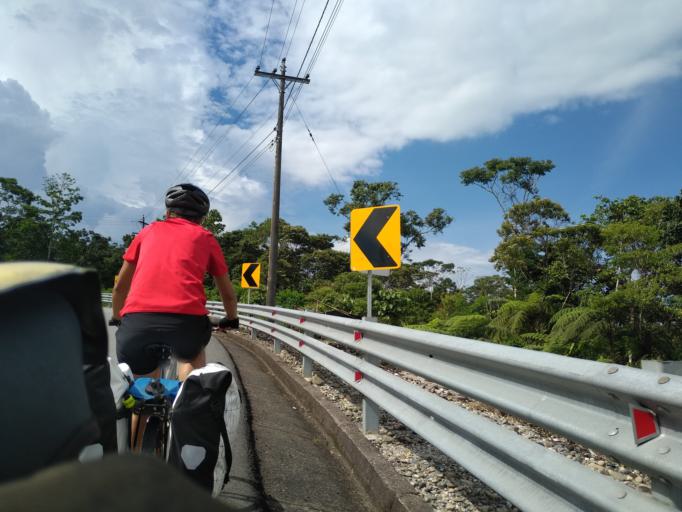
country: EC
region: Napo
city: Tena
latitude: -1.0888
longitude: -77.7891
